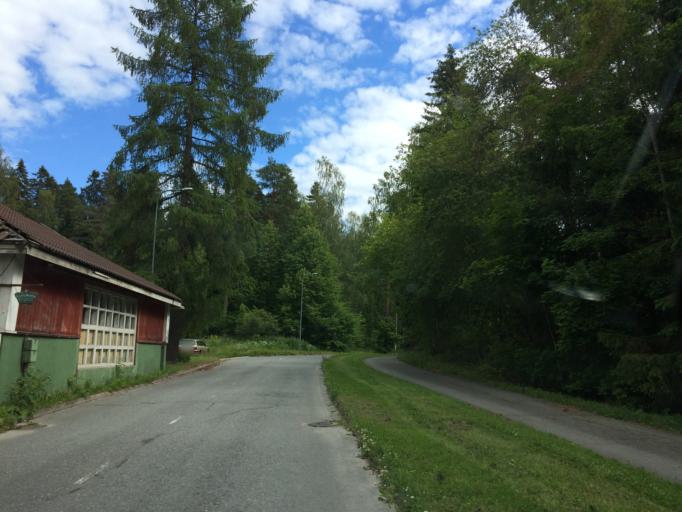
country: FI
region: Haeme
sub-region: Haemeenlinna
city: Tervakoski
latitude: 60.8147
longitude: 24.6186
